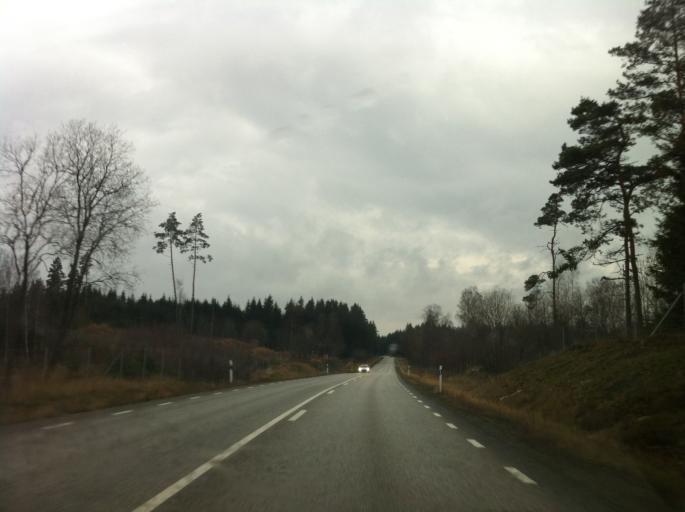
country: SE
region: Joenkoeping
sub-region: Savsjo Kommun
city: Stockaryd
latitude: 57.3823
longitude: 14.5822
